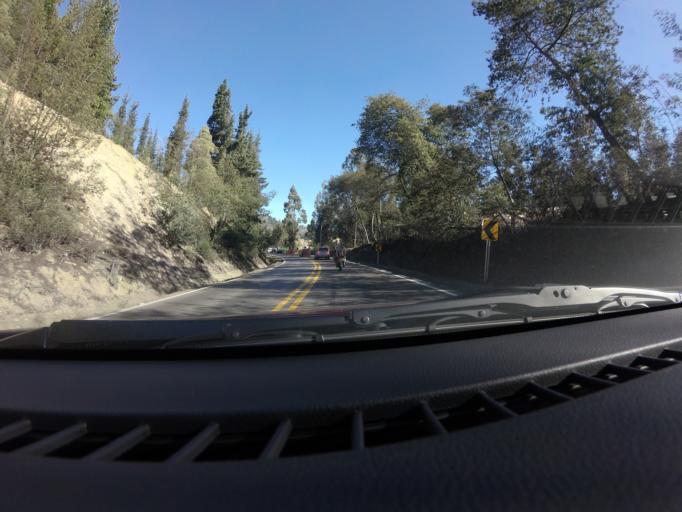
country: CO
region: Cundinamarca
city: Sutatausa
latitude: 5.2441
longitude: -73.8543
